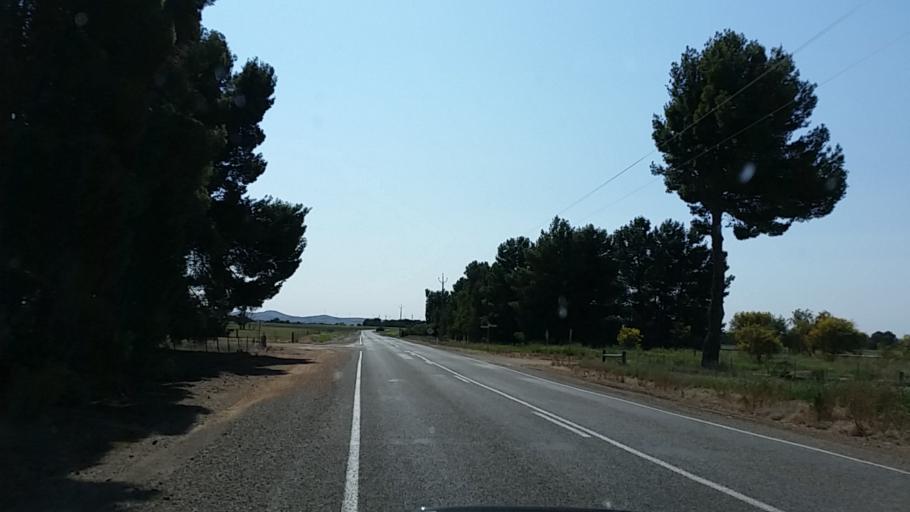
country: AU
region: South Australia
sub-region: Northern Areas
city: Jamestown
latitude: -33.1866
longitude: 138.4664
